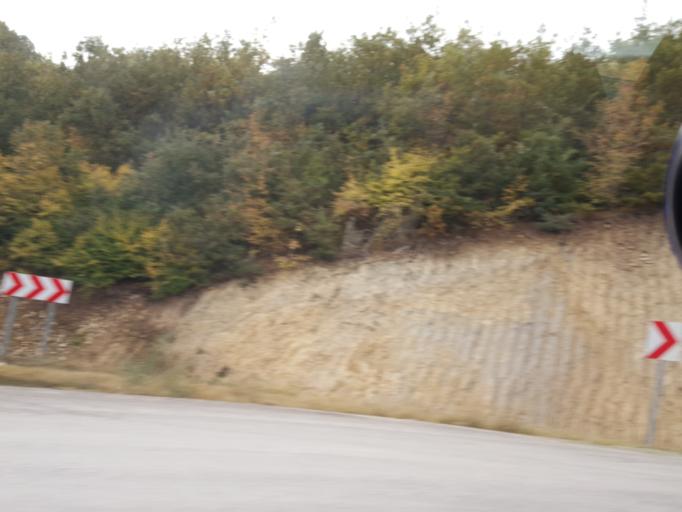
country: TR
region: Amasya
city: Gediksaray
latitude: 40.4603
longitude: 35.7784
